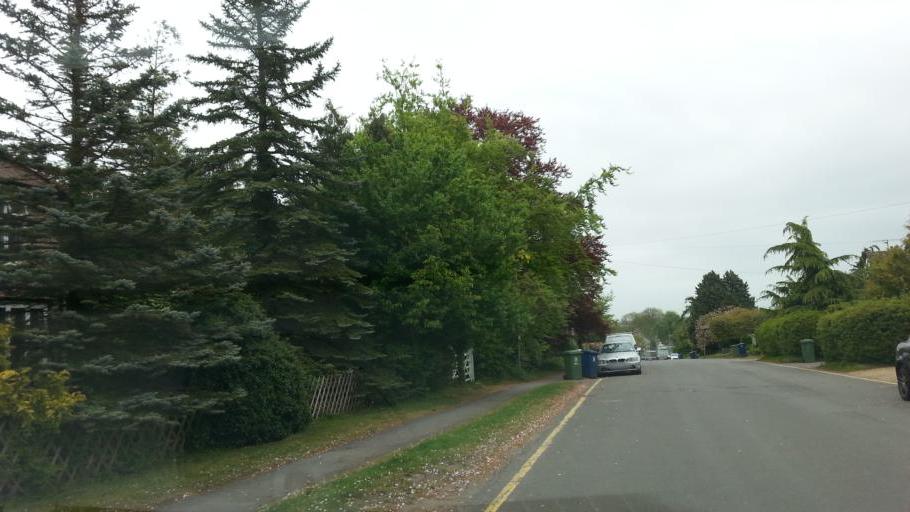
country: GB
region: England
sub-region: Cambridgeshire
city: Duxford
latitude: 52.1038
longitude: 0.1629
